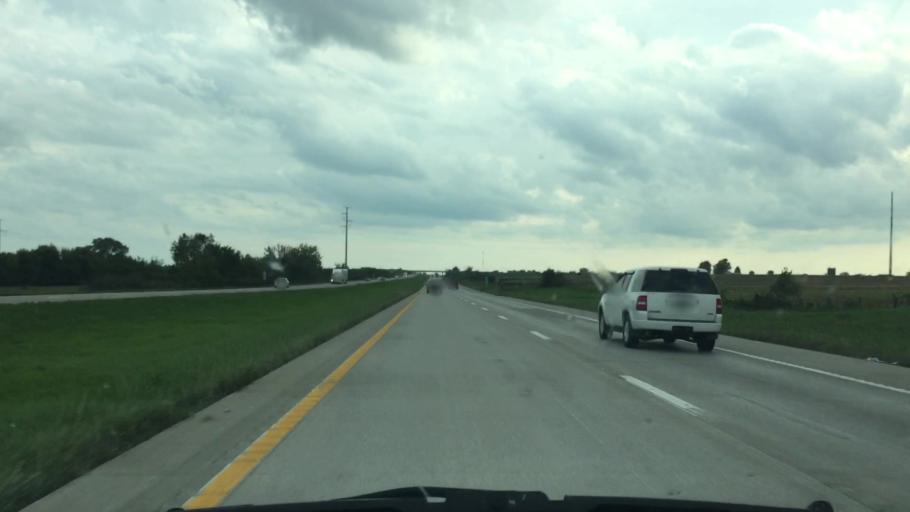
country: US
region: Missouri
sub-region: Clinton County
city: Cameron
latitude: 39.6406
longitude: -94.2429
